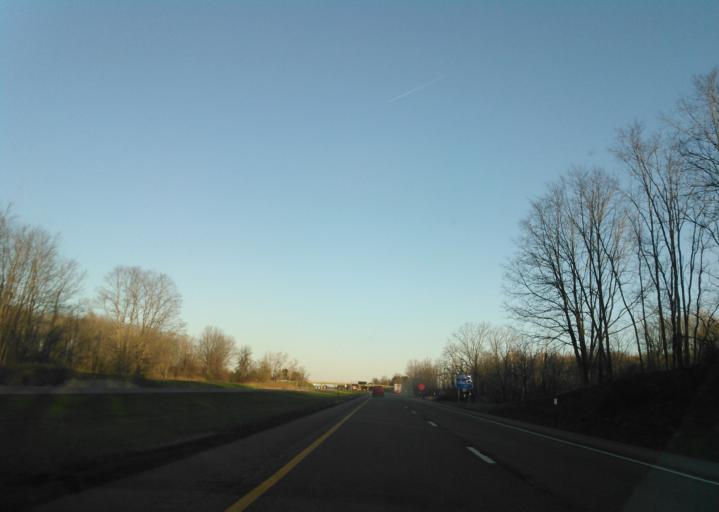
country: US
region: New York
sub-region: Monroe County
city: Pittsford
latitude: 43.0253
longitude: -77.5036
